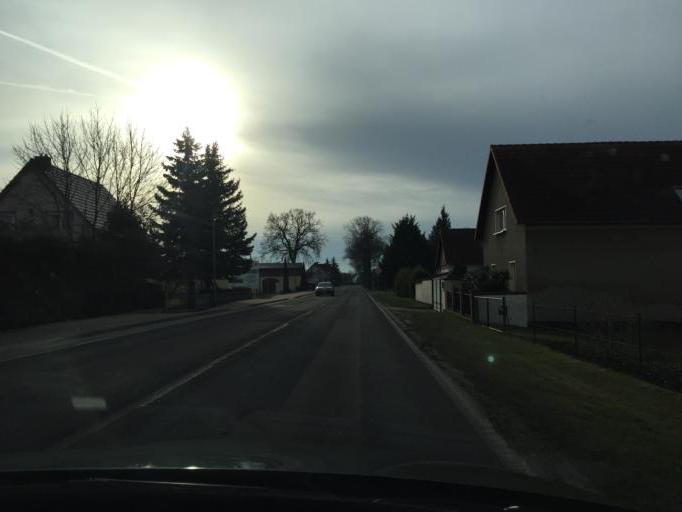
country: DE
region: Brandenburg
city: Peitz
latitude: 51.8681
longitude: 14.4180
